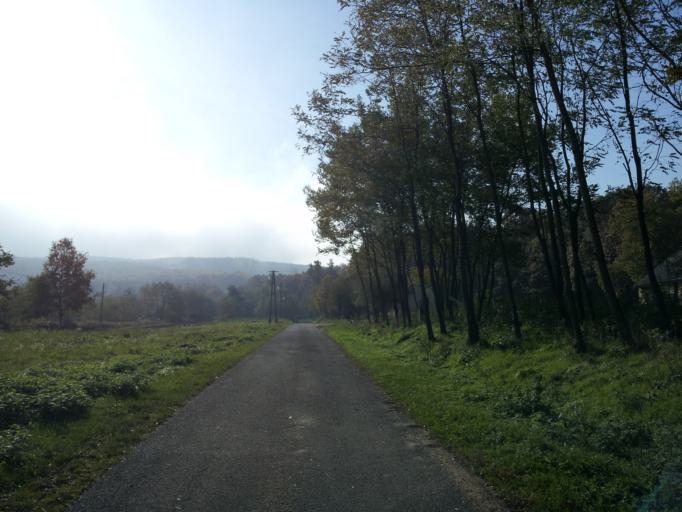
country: HU
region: Gyor-Moson-Sopron
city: Bakonyszentlaszlo
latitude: 47.3642
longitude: 17.8191
